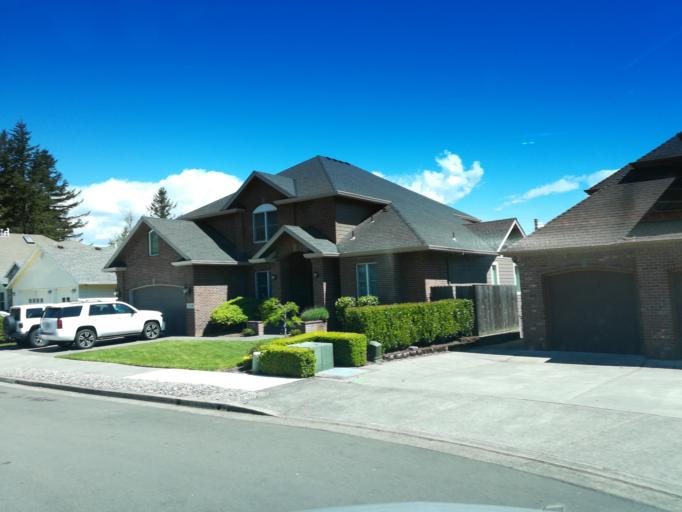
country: US
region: Oregon
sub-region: Multnomah County
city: Troutdale
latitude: 45.5183
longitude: -122.3732
